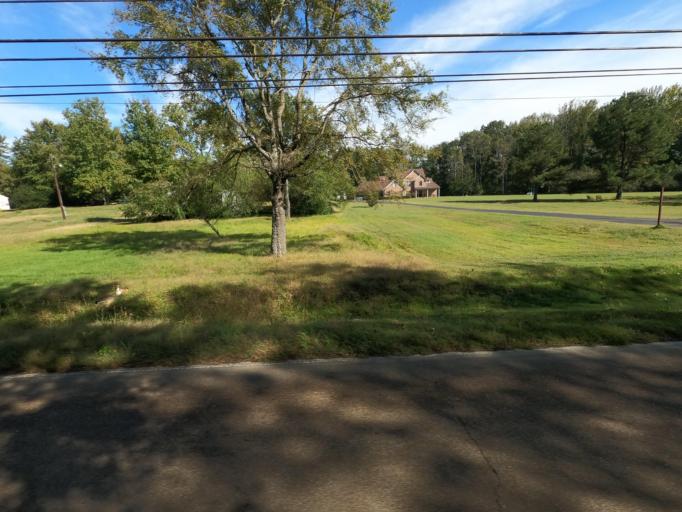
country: US
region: Tennessee
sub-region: Fayette County
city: Hickory Withe
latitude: 35.2340
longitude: -89.6499
